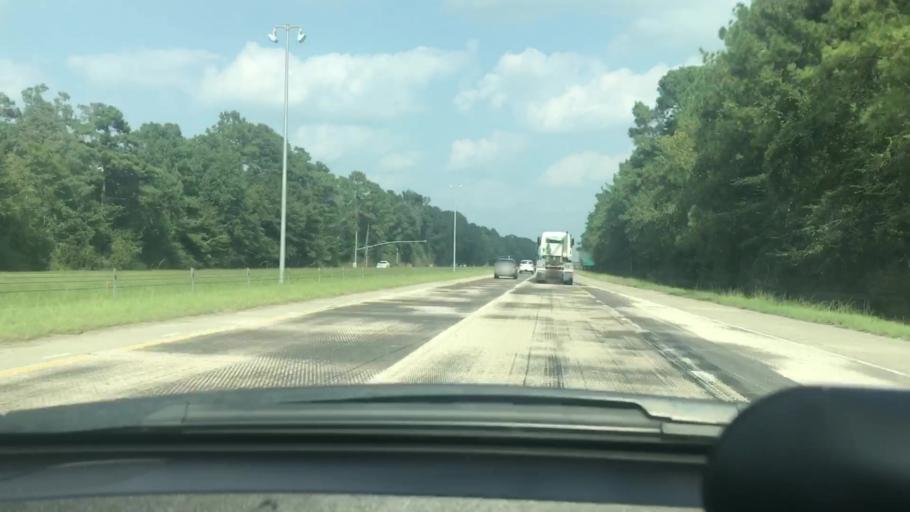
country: US
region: Louisiana
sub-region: Tangipahoa Parish
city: Hammond
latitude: 30.4794
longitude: -90.5146
